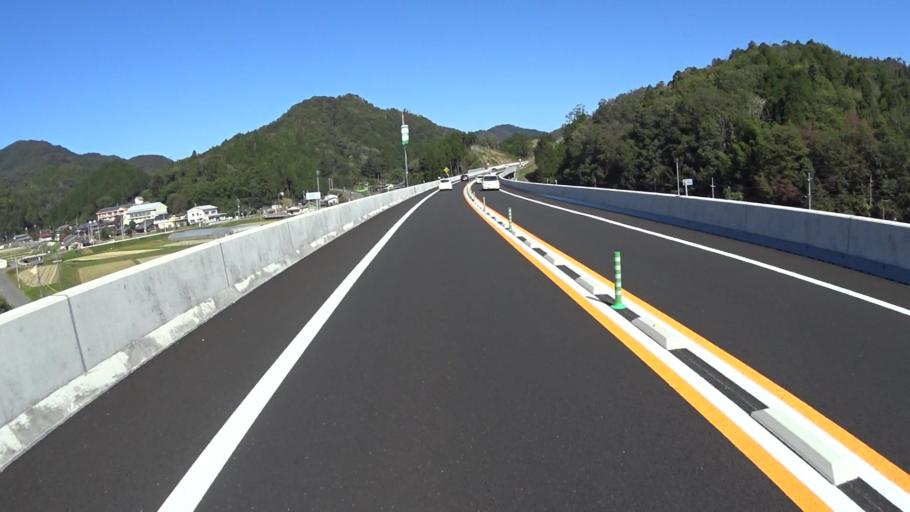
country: JP
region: Kyoto
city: Ayabe
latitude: 35.2170
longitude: 135.3424
